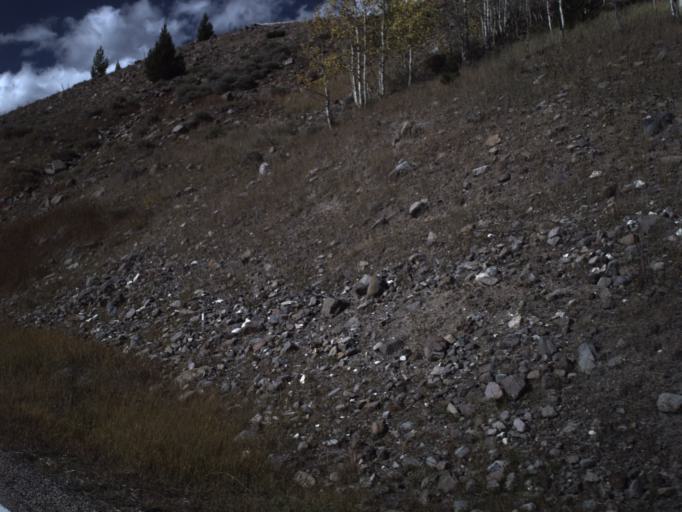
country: US
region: Utah
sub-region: Iron County
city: Parowan
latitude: 37.6641
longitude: -112.7194
